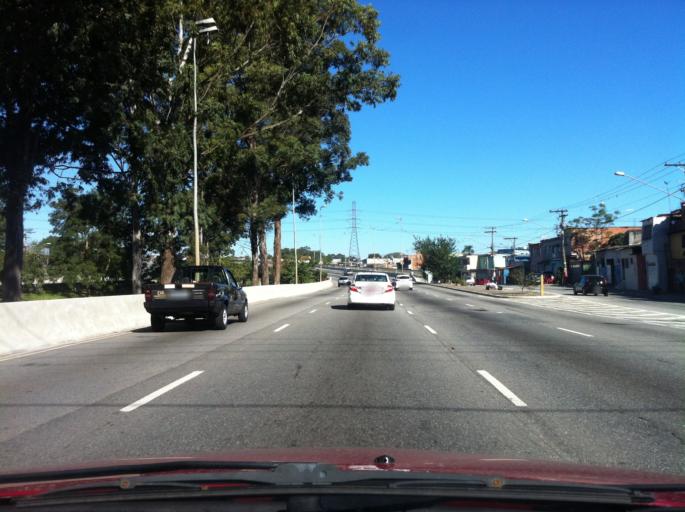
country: BR
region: Sao Paulo
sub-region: Guarulhos
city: Guarulhos
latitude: -23.5115
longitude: -46.4573
